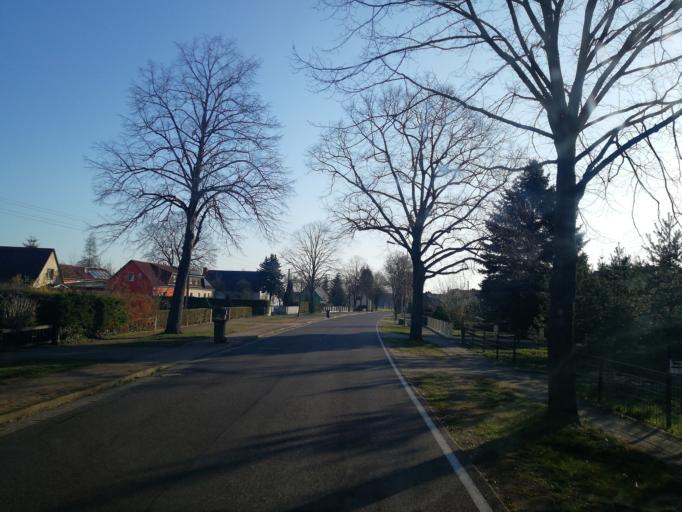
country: DE
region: Brandenburg
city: Drahnsdorf
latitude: 51.9203
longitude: 13.5982
